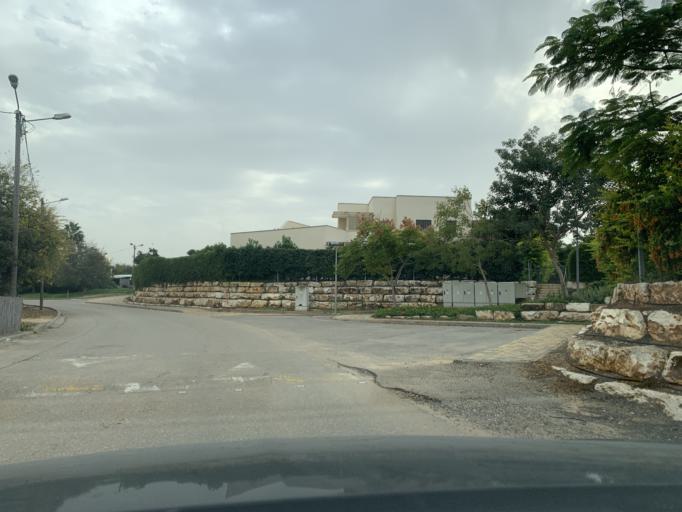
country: IL
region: Central District
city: Tirah
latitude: 32.2187
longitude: 34.9406
